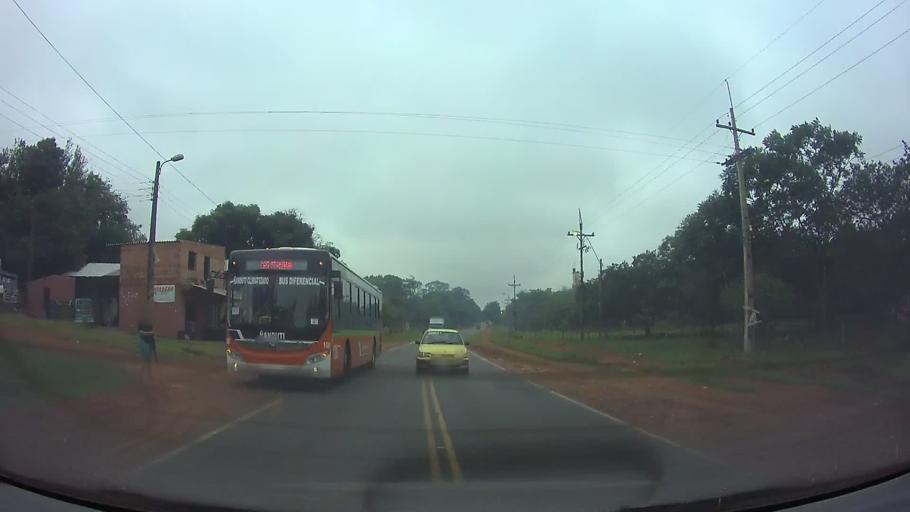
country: PY
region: Central
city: Itaugua
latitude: -25.4189
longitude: -57.3624
